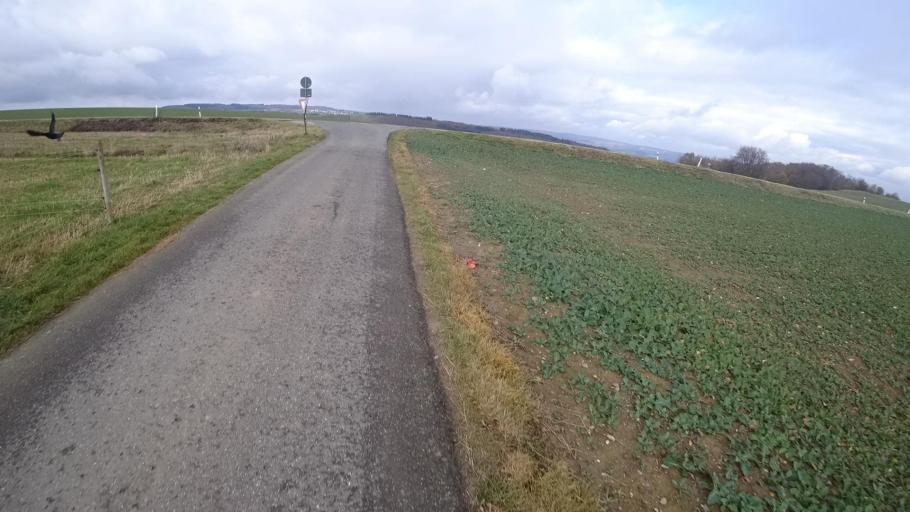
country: DE
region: Rheinland-Pfalz
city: Utzenhain
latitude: 50.1264
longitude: 7.6264
